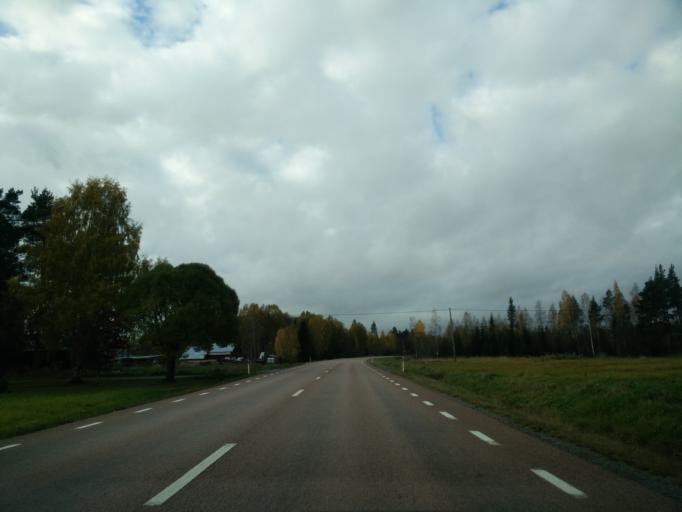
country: SE
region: Vaesternorrland
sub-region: Ange Kommun
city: Ange
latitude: 62.5108
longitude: 15.5691
